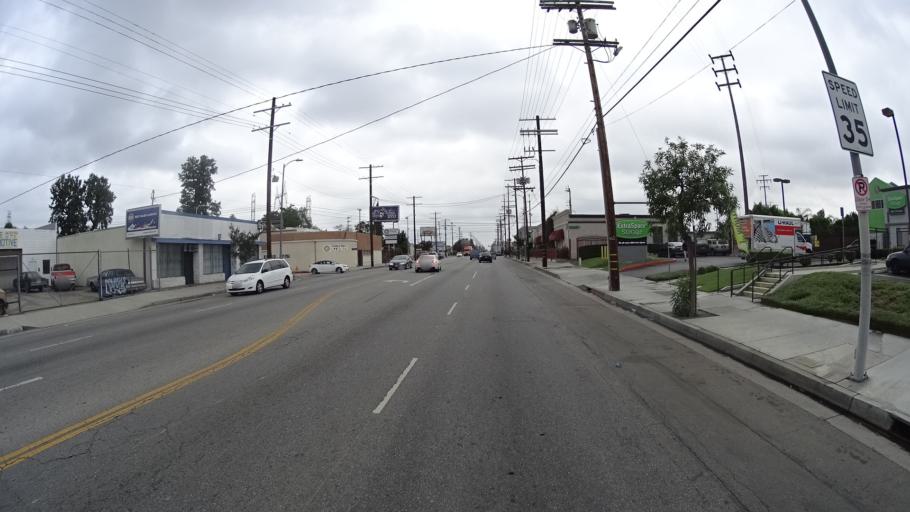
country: US
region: California
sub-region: Los Angeles County
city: North Hollywood
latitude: 34.1940
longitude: -118.3796
